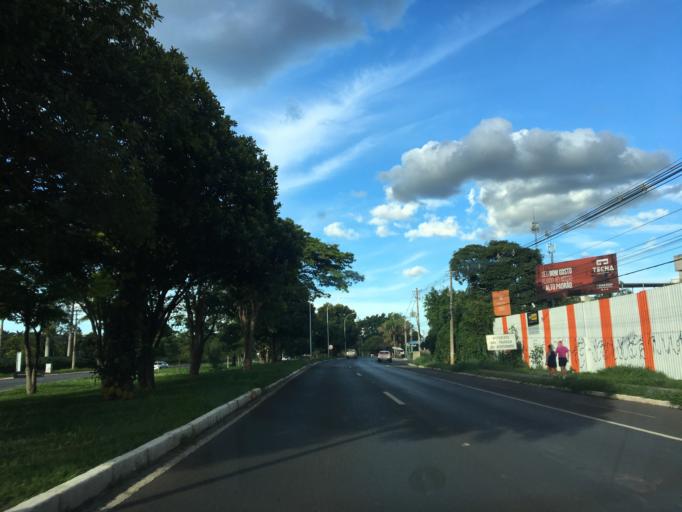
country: BR
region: Federal District
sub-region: Brasilia
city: Brasilia
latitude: -15.8524
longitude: -47.9122
